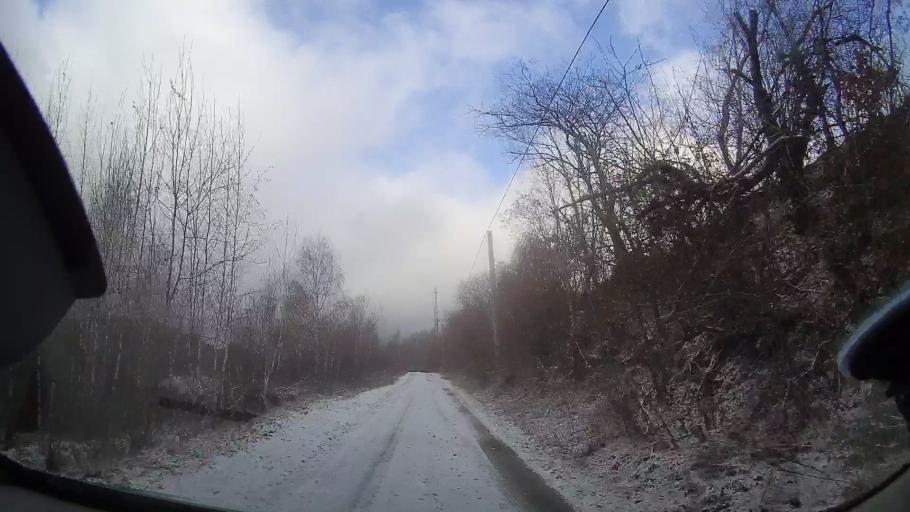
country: RO
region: Cluj
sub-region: Comuna Valea Ierii
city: Valea Ierii
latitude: 46.6536
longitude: 23.3521
